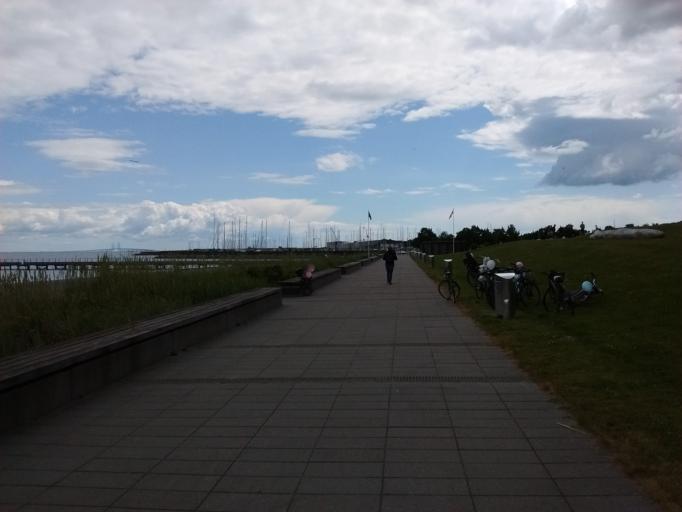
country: DK
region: Capital Region
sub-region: Tarnby Kommune
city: Tarnby
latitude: 55.6458
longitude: 12.6471
